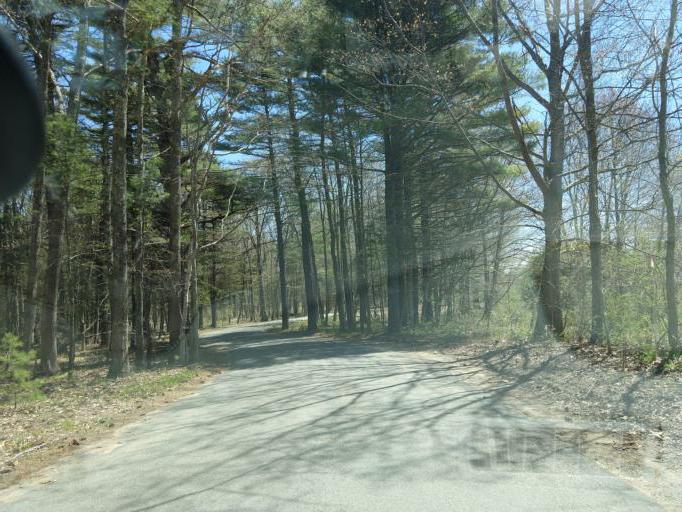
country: US
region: Maine
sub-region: York County
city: Wells Beach Station
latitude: 43.3414
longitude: -70.5541
